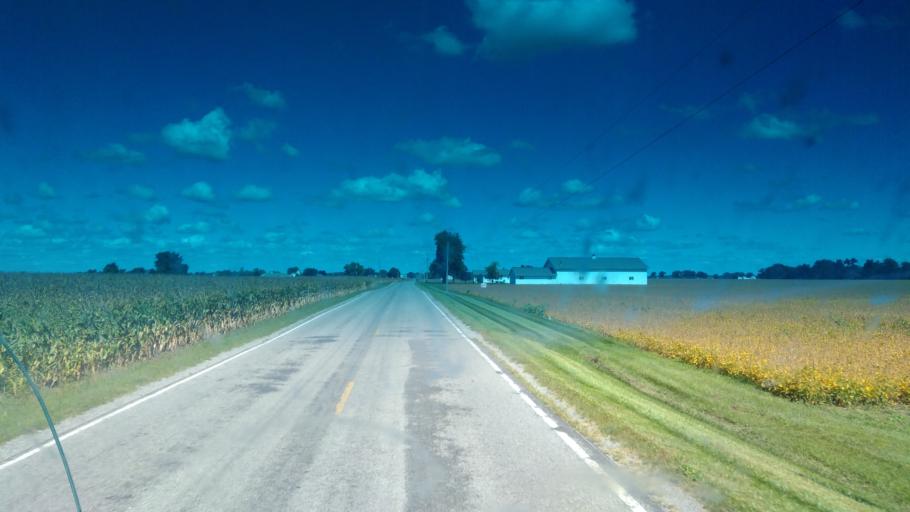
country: US
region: Ohio
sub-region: Madison County
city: Plain City
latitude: 40.0477
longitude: -83.3501
